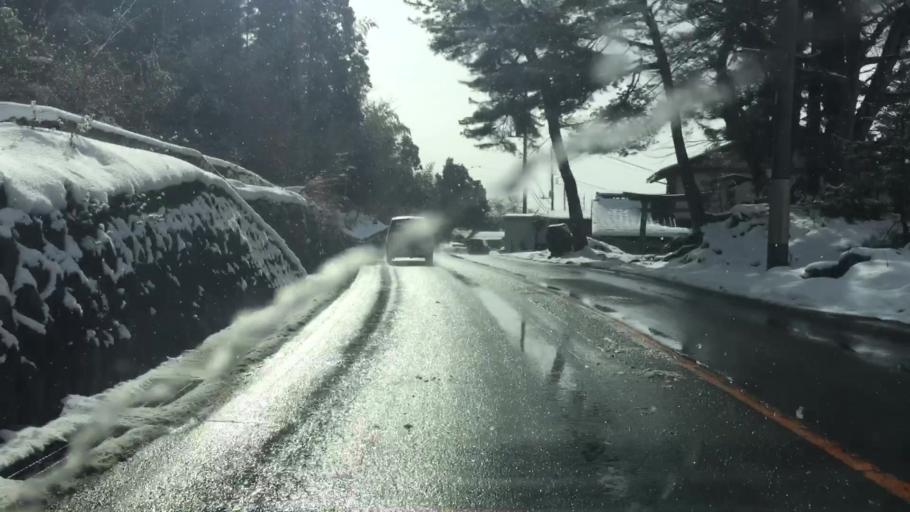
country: JP
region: Gunma
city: Numata
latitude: 36.6732
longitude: 139.0628
